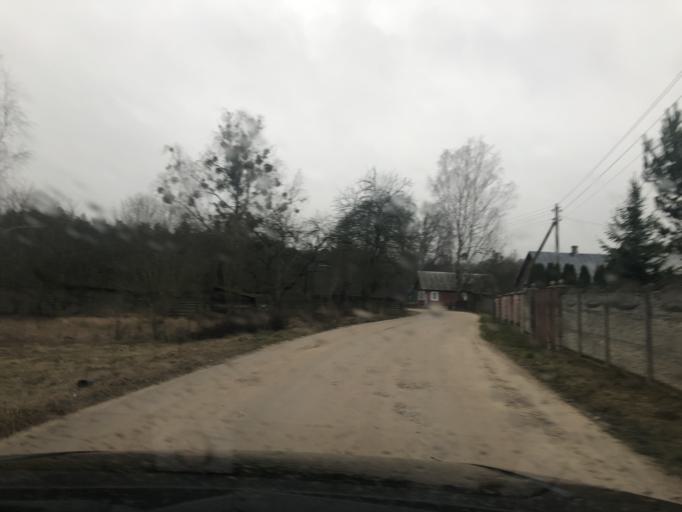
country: BY
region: Grodnenskaya
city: Skidal'
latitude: 53.8581
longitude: 24.2512
